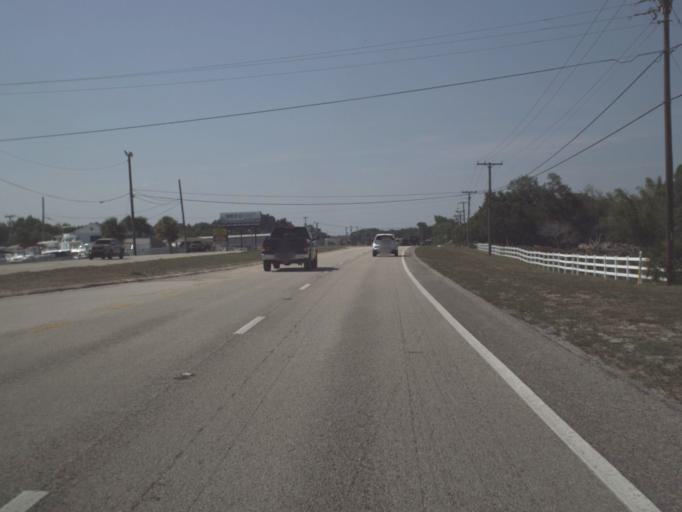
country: US
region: Florida
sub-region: Brevard County
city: Rockledge
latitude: 28.3149
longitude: -80.7107
